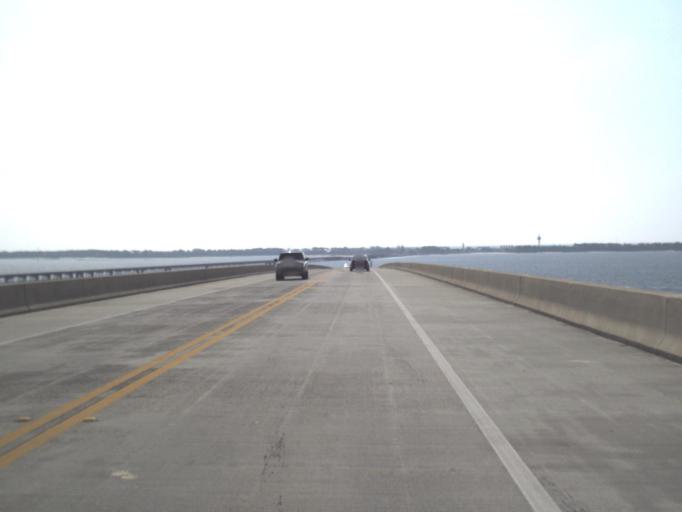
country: US
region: Florida
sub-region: Franklin County
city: Eastpoint
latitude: 29.6830
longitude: -84.8796
